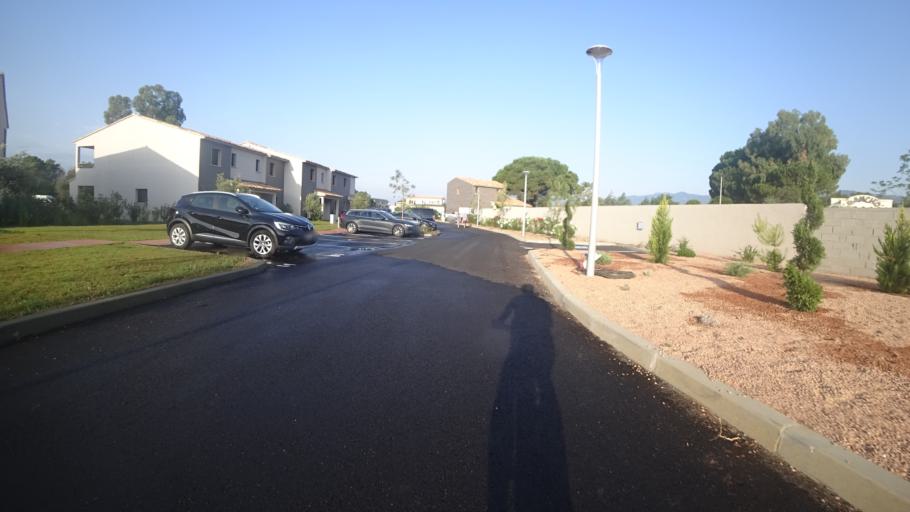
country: FR
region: Corsica
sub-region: Departement de la Corse-du-Sud
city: Porto-Vecchio
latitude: 41.6287
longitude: 9.3356
